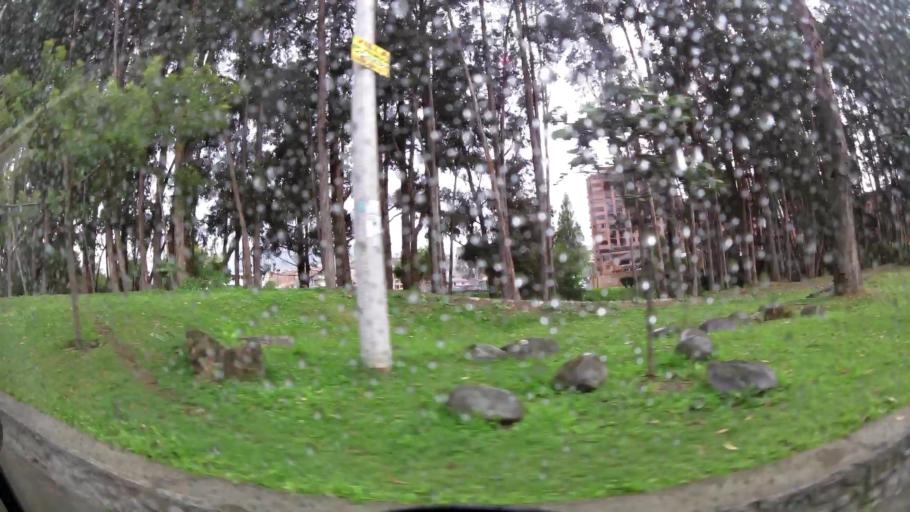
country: EC
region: Azuay
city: Cuenca
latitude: -2.8906
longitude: -79.0343
